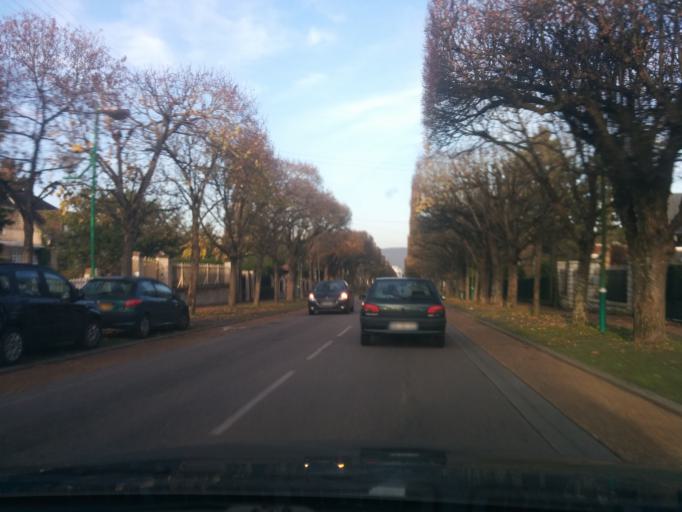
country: FR
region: Haute-Normandie
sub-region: Departement de l'Eure
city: Vernon
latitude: 49.0843
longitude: 1.4785
